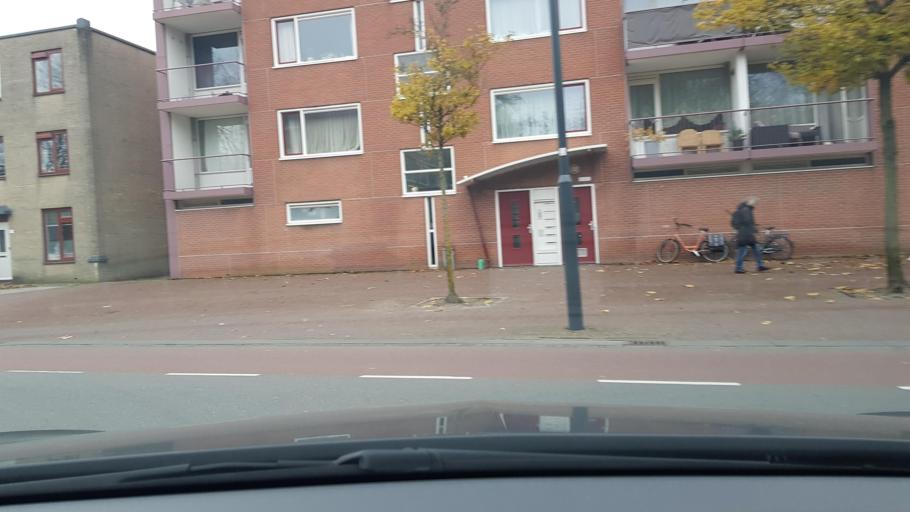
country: NL
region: North Holland
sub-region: Gemeente Haarlem
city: Haarlem
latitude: 52.3572
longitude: 4.6644
